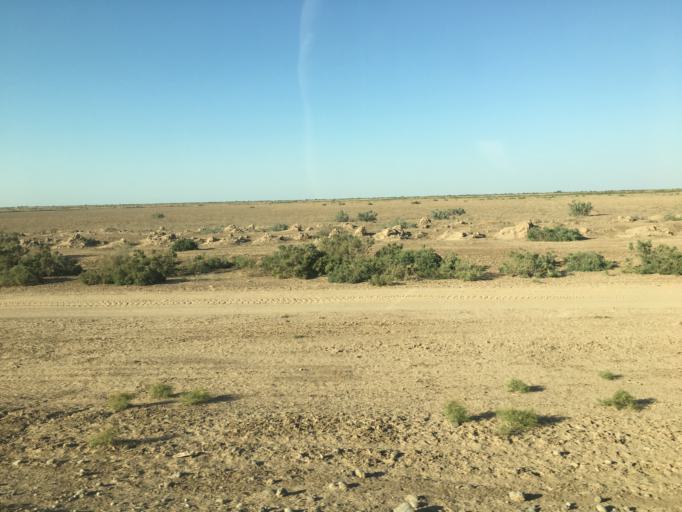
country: IR
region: Razavi Khorasan
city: Sarakhs
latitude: 37.0460
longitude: 61.3010
